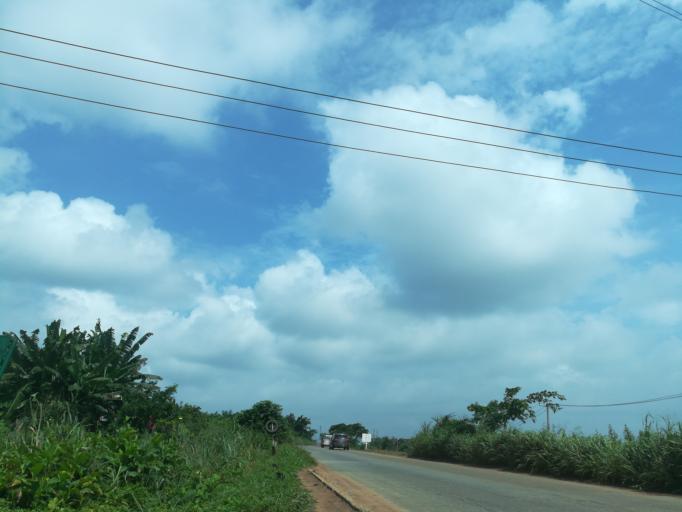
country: NG
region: Lagos
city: Ikorodu
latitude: 6.6607
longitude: 3.6806
